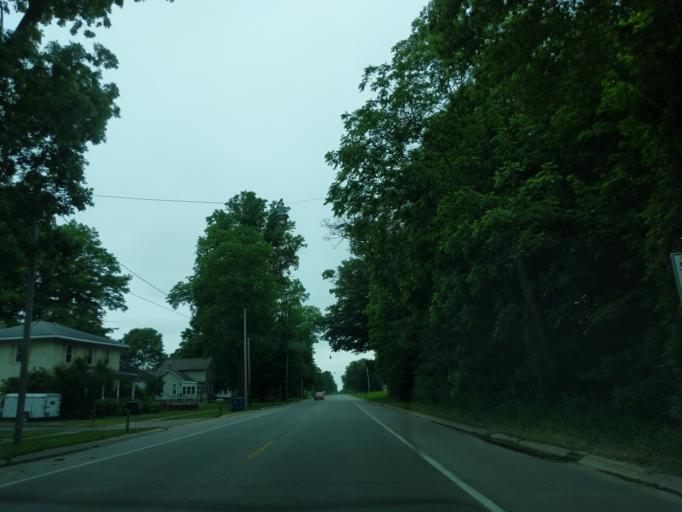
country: US
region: Michigan
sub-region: Hillsdale County
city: Litchfield
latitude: 41.9563
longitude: -84.7729
